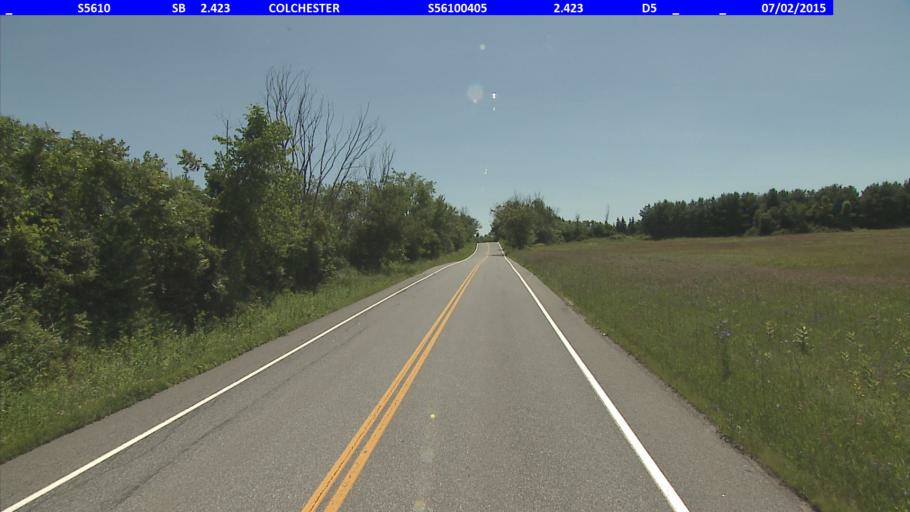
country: US
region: Vermont
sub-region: Chittenden County
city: Colchester
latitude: 44.5745
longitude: -73.1272
